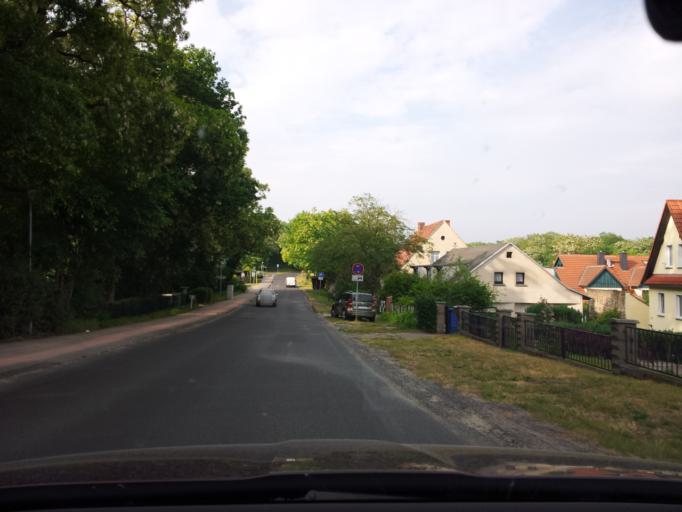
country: DE
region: Brandenburg
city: Werder
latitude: 52.3472
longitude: 12.9459
